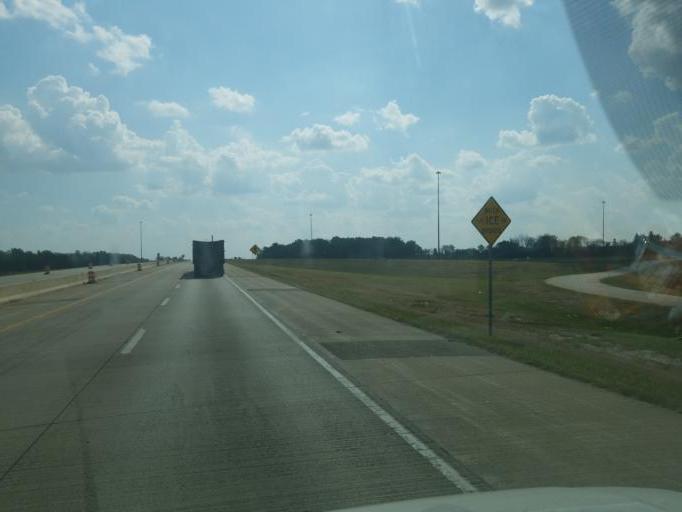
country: US
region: Indiana
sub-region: Allen County
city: New Haven
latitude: 41.0668
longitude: -84.9898
